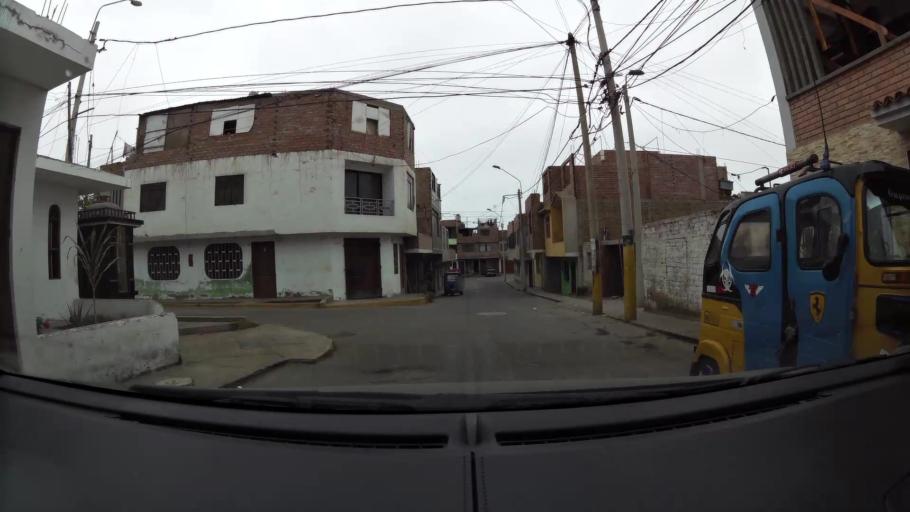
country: PE
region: Lima
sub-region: Barranca
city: Barranca
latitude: -10.7514
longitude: -77.7544
